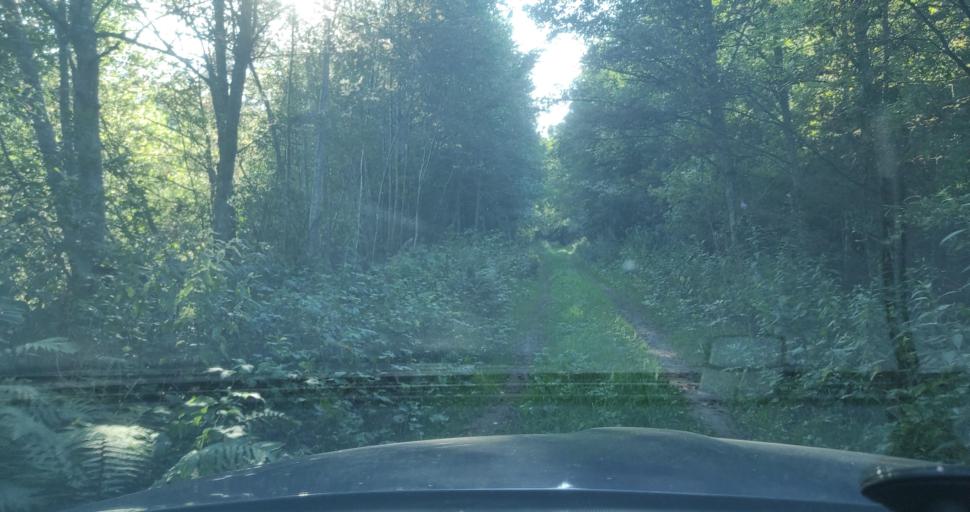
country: LV
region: Skrunda
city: Skrunda
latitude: 56.6795
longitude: 21.9774
